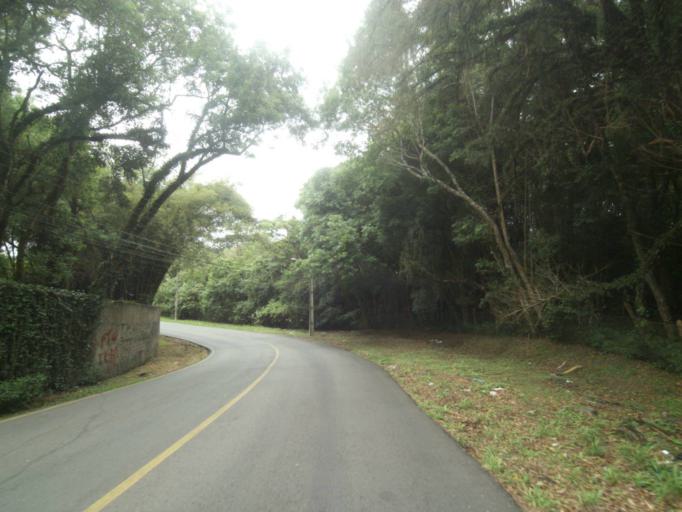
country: BR
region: Parana
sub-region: Curitiba
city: Curitiba
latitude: -25.3975
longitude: -49.2870
